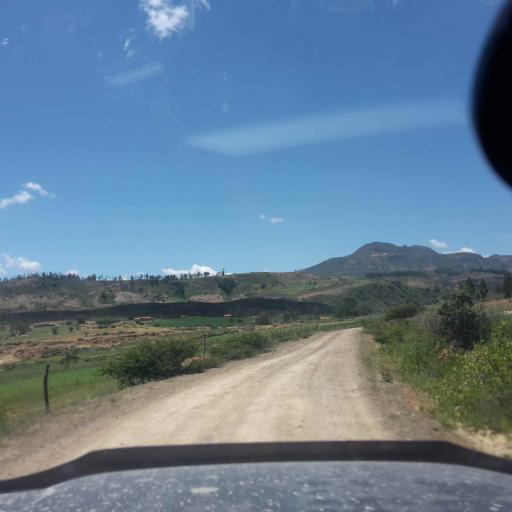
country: BO
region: Cochabamba
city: Totora
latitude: -17.7742
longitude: -65.2515
